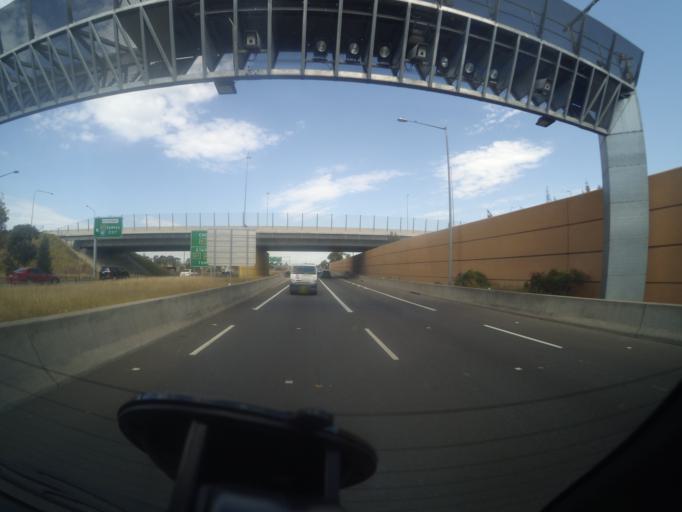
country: AU
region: New South Wales
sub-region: Liverpool
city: Miller
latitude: -33.9432
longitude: 150.8783
